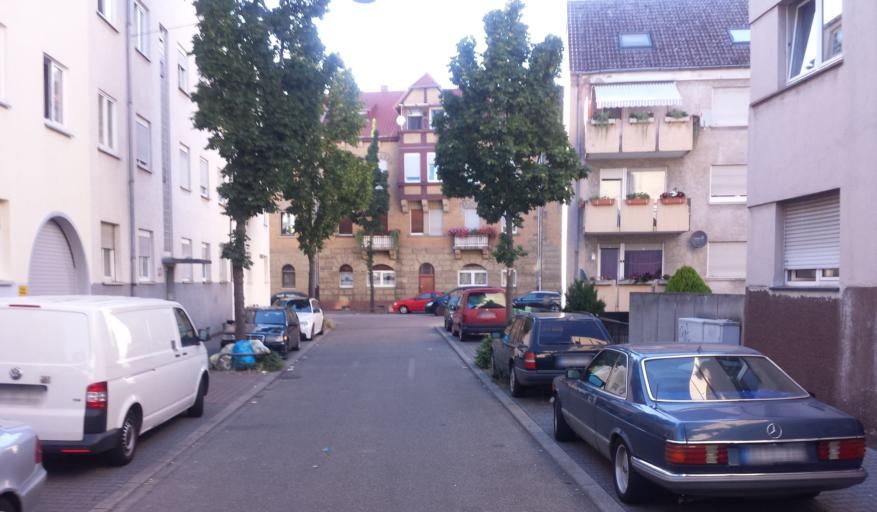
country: DE
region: Baden-Wuerttemberg
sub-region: Karlsruhe Region
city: Mannheim
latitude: 49.5277
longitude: 8.4799
